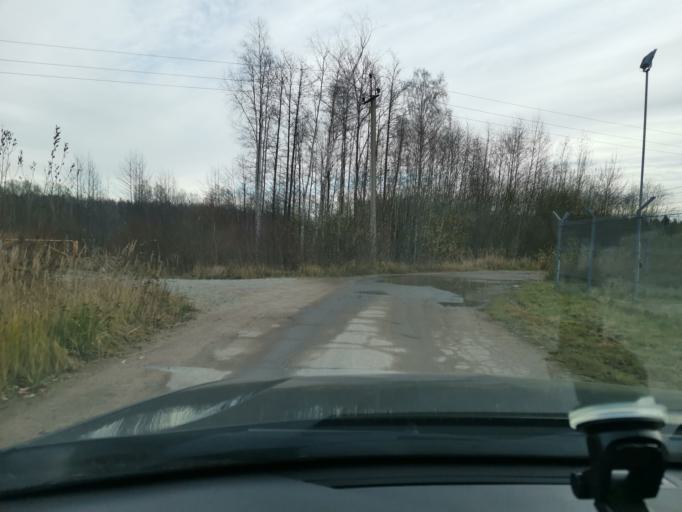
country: EE
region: Ida-Virumaa
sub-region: Sillamaee linn
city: Sillamae
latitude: 59.2604
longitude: 27.9105
